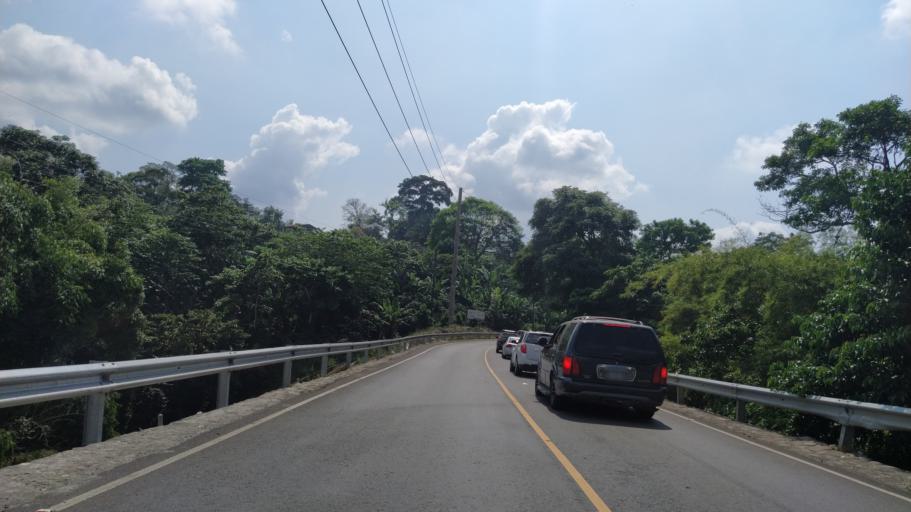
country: GT
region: Quetzaltenango
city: El Palmar
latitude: 14.6402
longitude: -91.5756
